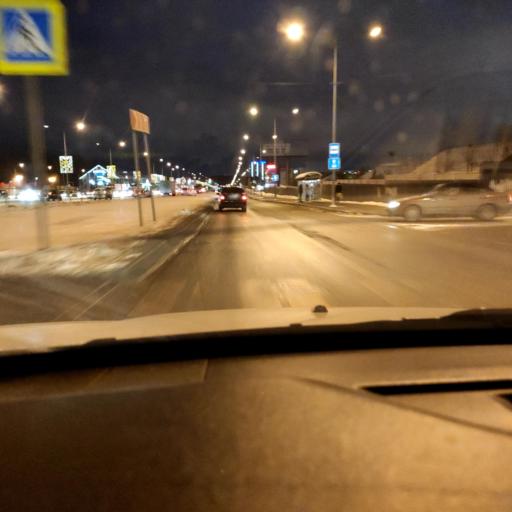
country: RU
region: Samara
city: Petra-Dubrava
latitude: 53.2962
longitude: 50.2851
